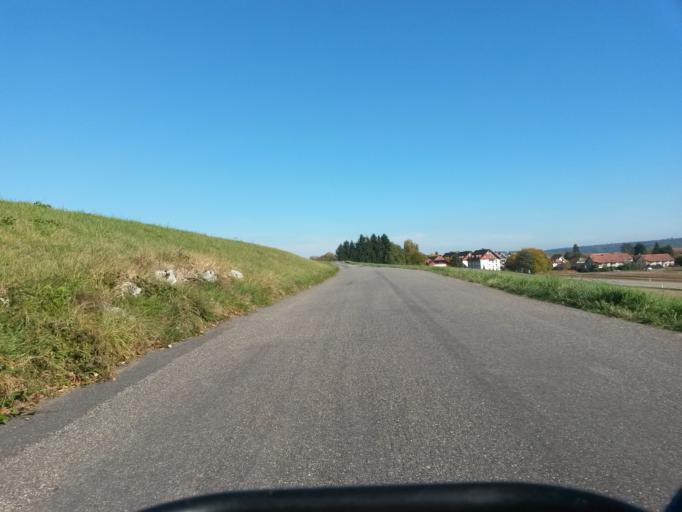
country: CH
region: Solothurn
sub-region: Bezirk Lebern
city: Selzach
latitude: 47.2017
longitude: 7.4454
